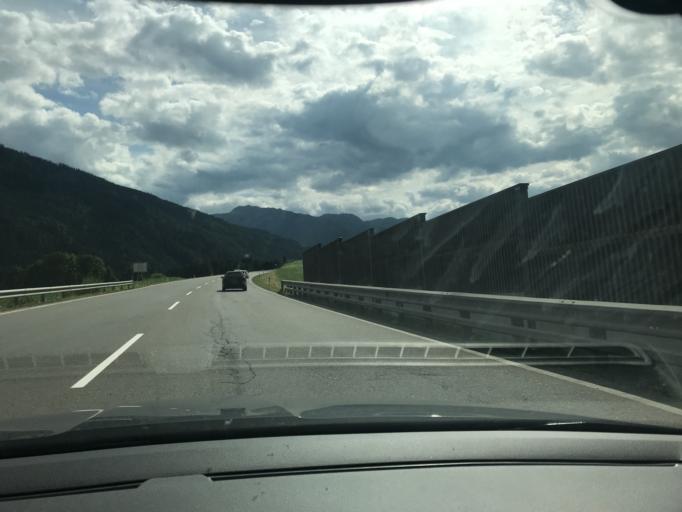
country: AT
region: Tyrol
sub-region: Politischer Bezirk Lienz
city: Strassen
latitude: 46.7556
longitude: 12.5119
